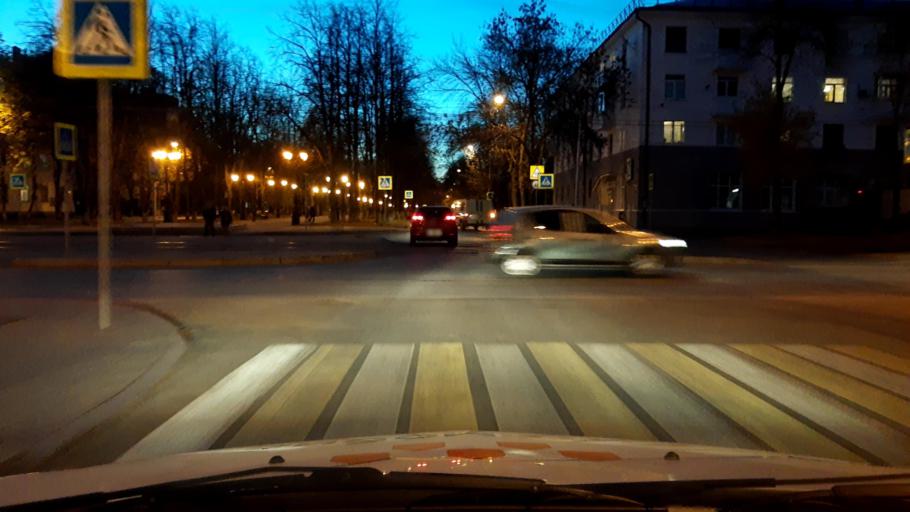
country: RU
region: Bashkortostan
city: Ufa
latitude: 54.8205
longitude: 56.0652
